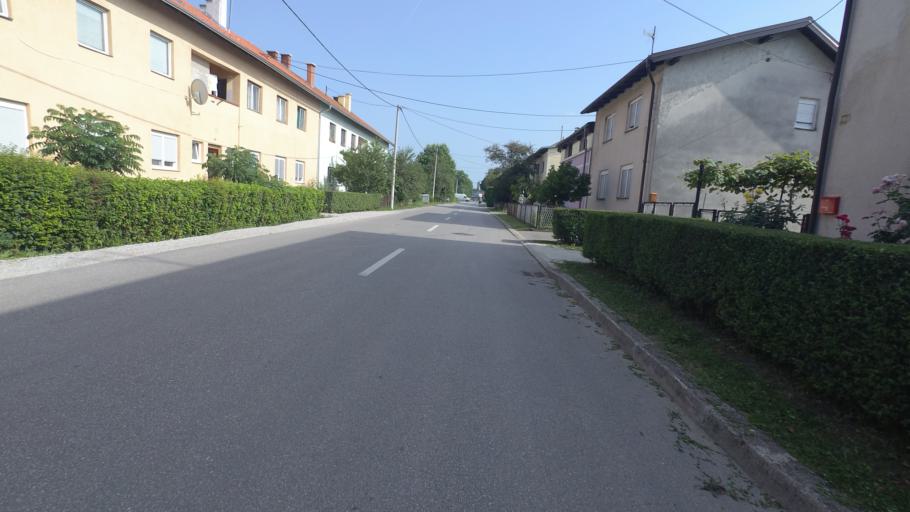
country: HR
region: Karlovacka
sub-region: Grad Karlovac
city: Karlovac
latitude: 45.4982
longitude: 15.5430
